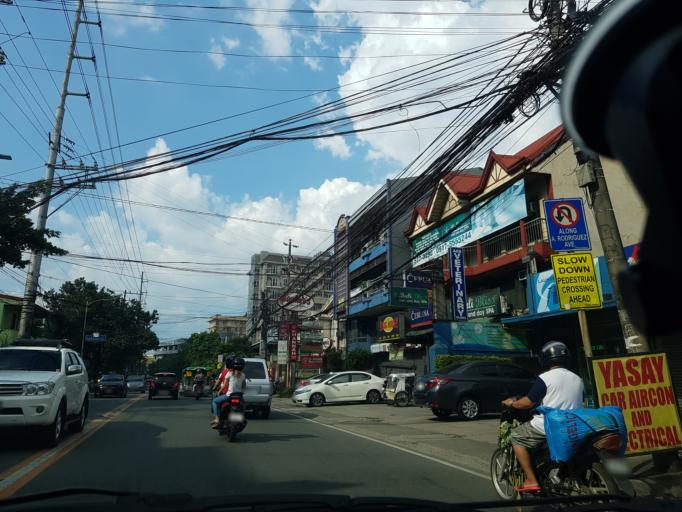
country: PH
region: Metro Manila
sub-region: Marikina
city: Calumpang
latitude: 14.6063
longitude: 121.0922
